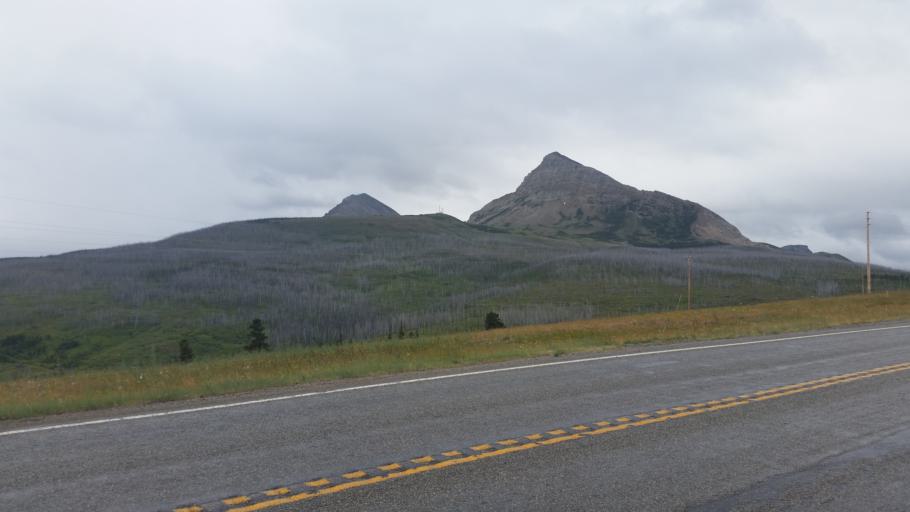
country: US
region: Montana
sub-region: Glacier County
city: North Browning
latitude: 48.6869
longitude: -113.3624
